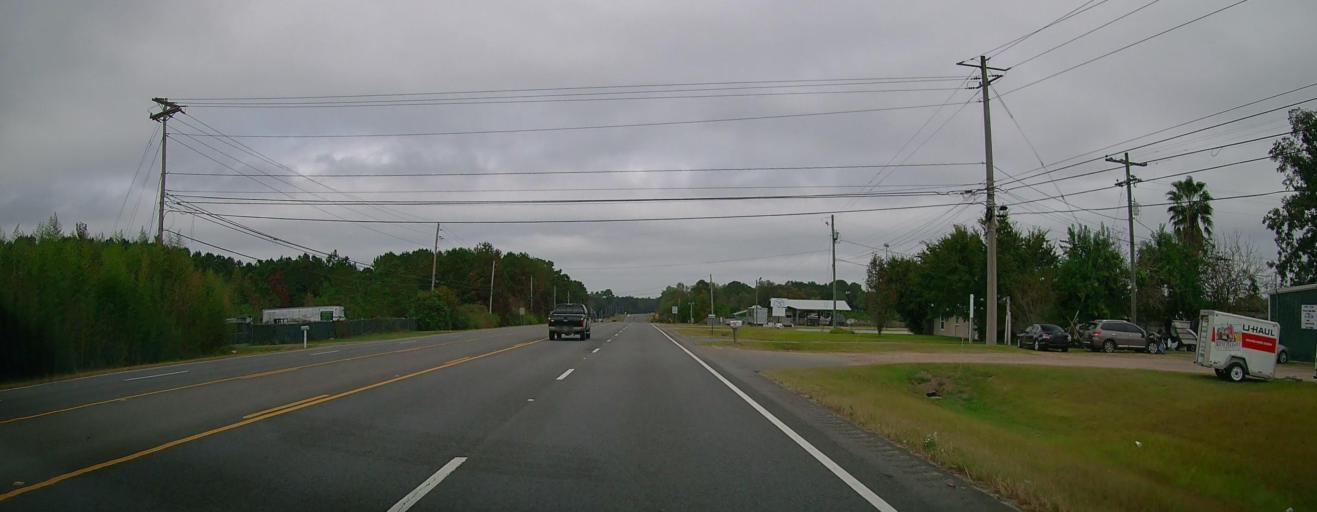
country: US
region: Georgia
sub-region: Thomas County
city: Thomasville
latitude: 30.8829
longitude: -83.9315
